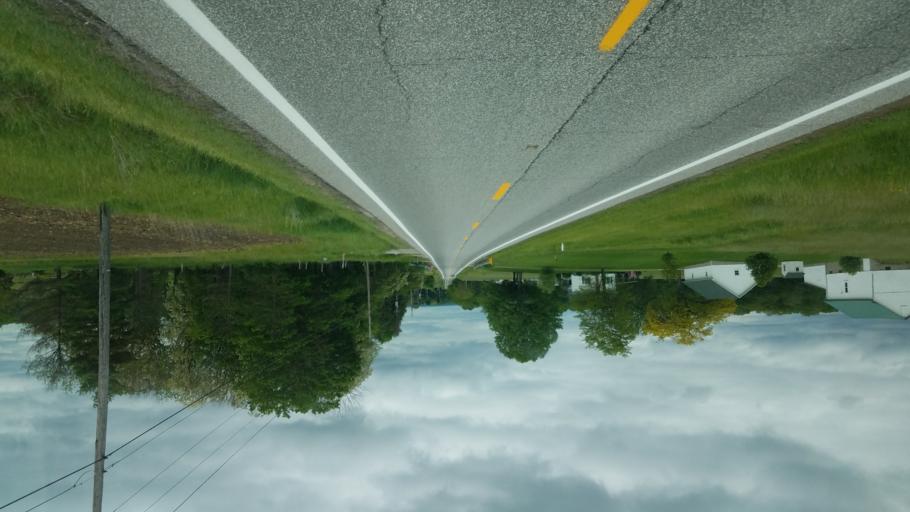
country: US
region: Ohio
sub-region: Geauga County
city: Middlefield
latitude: 41.3889
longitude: -81.0200
